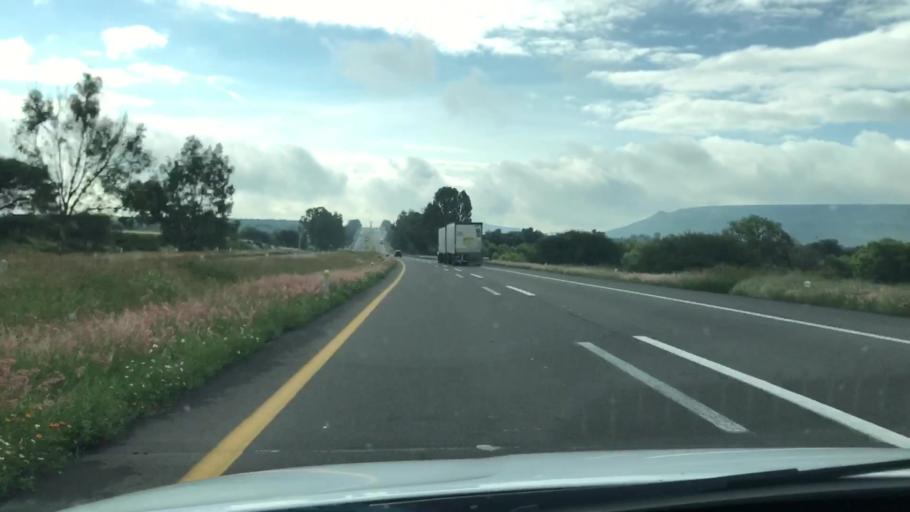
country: MX
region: Jalisco
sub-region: Lagos de Moreno
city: Cristeros [Fraccionamiento]
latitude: 21.2859
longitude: -102.0013
